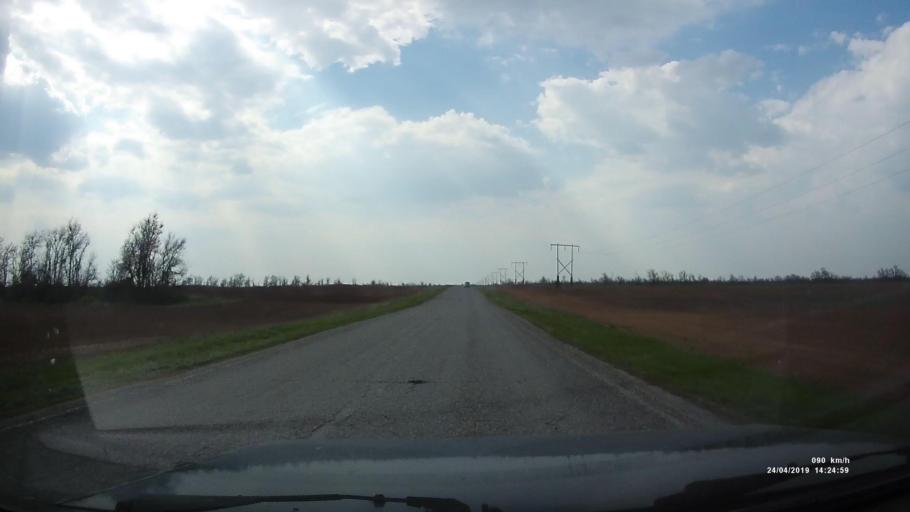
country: RU
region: Kalmykiya
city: Arshan'
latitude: 46.3297
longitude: 44.0873
